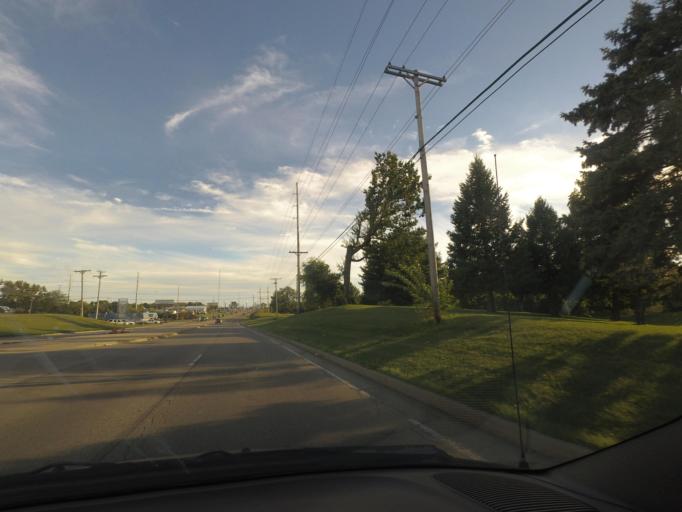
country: US
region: Illinois
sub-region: Sangamon County
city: Grandview
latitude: 39.8002
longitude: -89.6061
